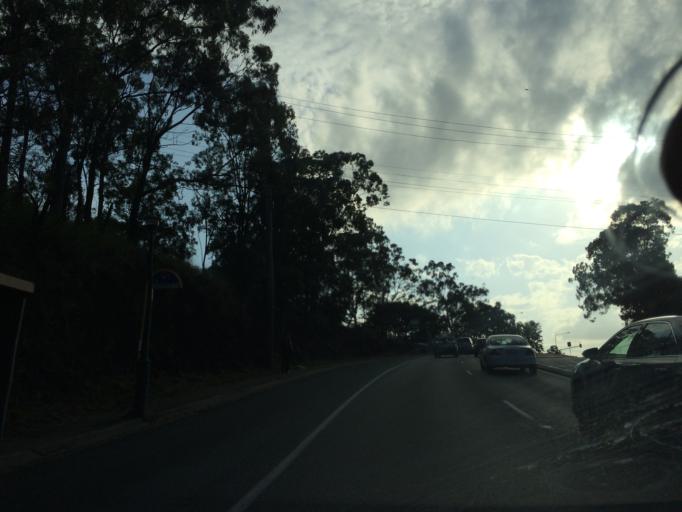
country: AU
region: Queensland
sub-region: Brisbane
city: Kenmore Hills
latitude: -27.5085
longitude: 152.9546
